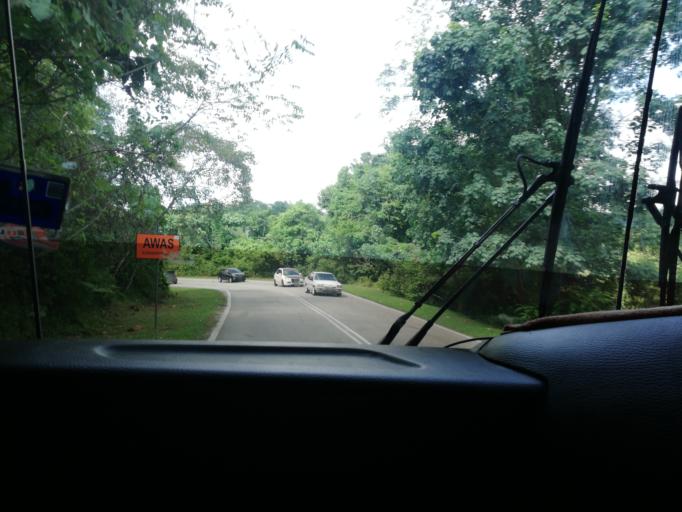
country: MY
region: Kedah
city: Kulim
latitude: 5.3412
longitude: 100.5887
